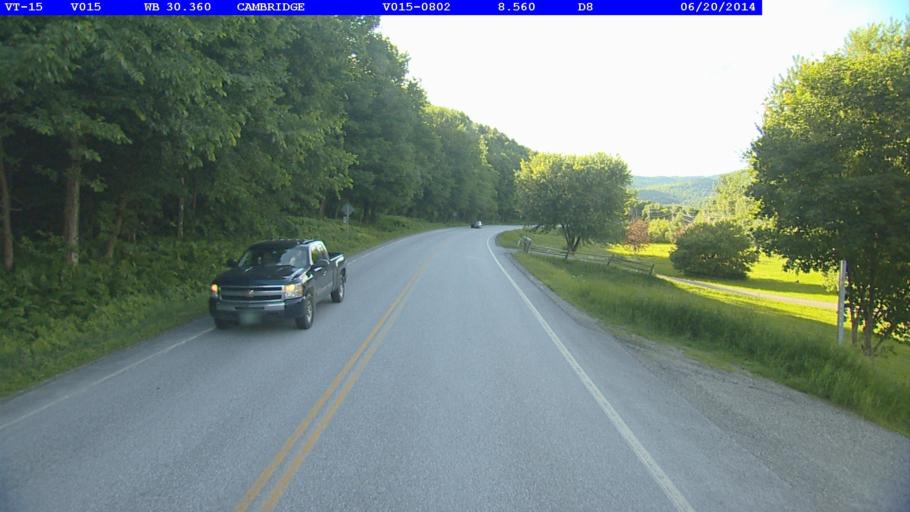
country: US
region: Vermont
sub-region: Lamoille County
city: Johnson
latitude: 44.6619
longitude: -72.7729
